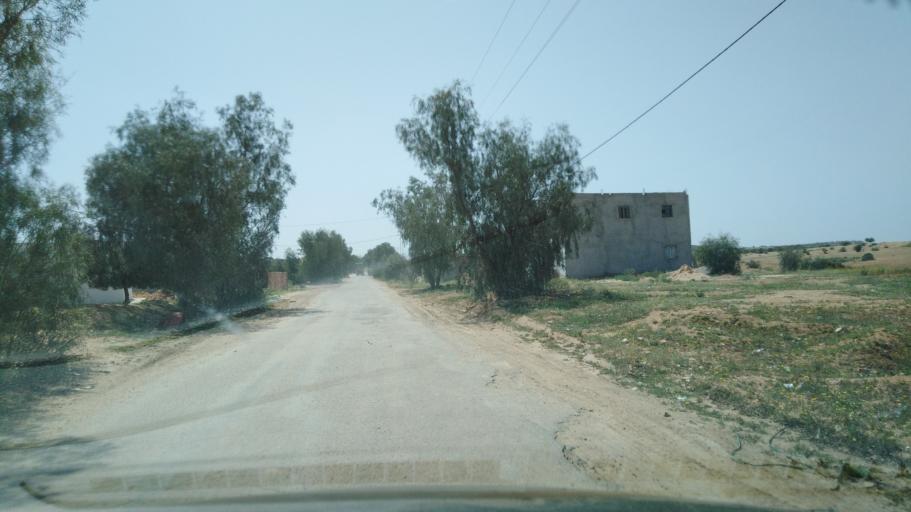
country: TN
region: Safaqis
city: Sfax
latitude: 34.7247
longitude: 10.5297
